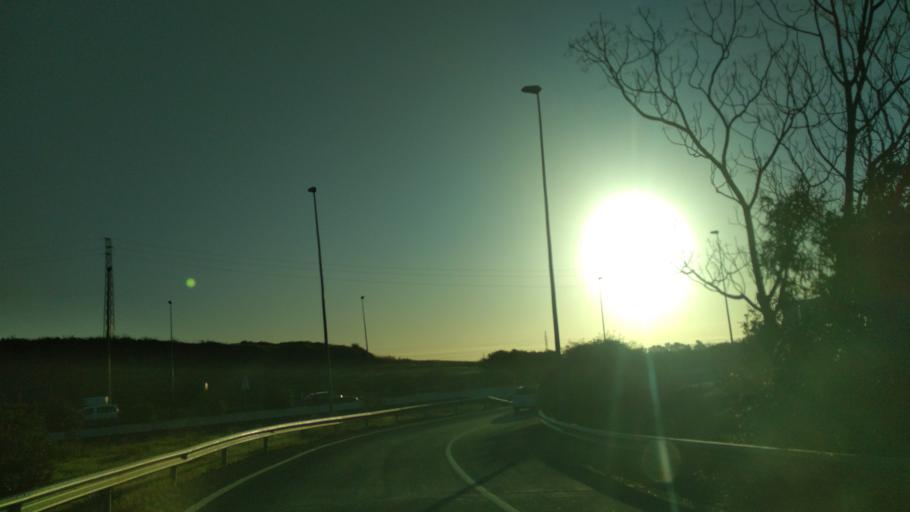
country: ES
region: Andalusia
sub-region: Provincia de Huelva
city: Huelva
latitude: 37.2760
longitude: -6.9215
